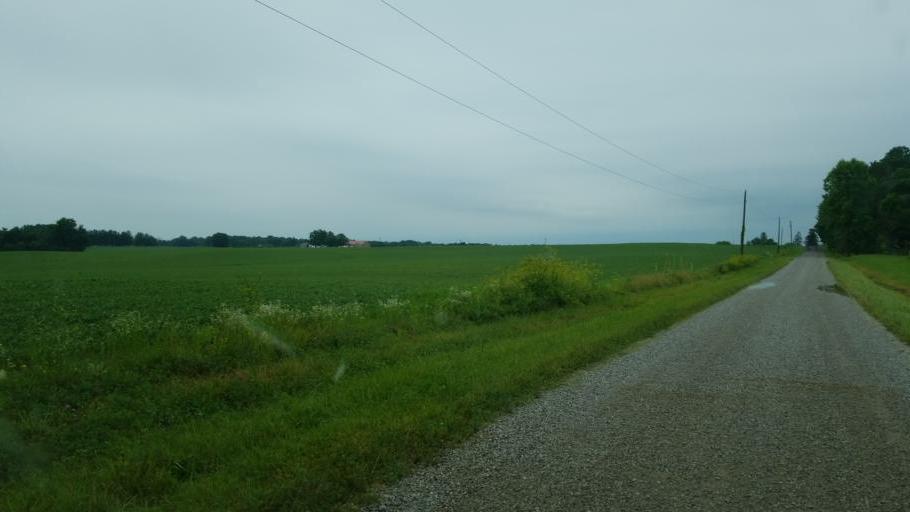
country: US
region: Ohio
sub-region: Knox County
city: Fredericktown
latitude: 40.4933
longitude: -82.6599
